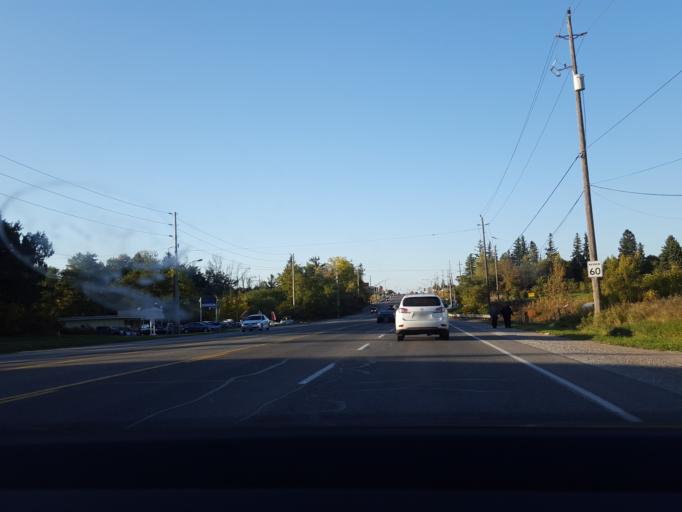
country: CA
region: Ontario
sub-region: York
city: Richmond Hill
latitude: 43.9198
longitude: -79.4486
